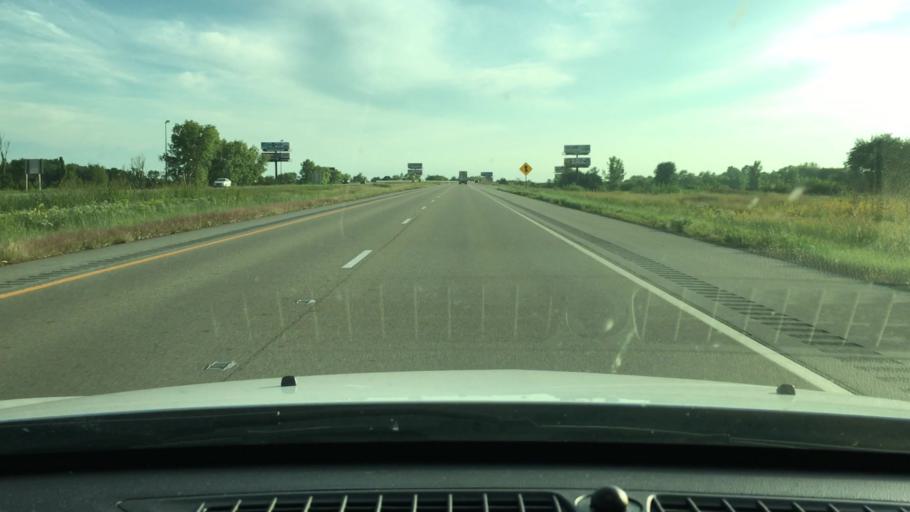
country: US
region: Illinois
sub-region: Logan County
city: Atlanta
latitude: 40.2583
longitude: -89.2218
